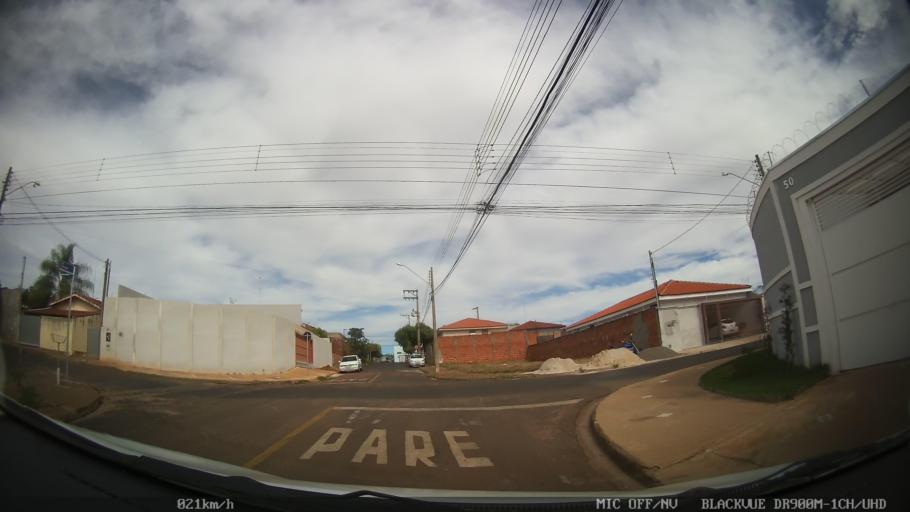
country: BR
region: Sao Paulo
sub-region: Catanduva
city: Catanduva
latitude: -21.1582
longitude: -48.9728
